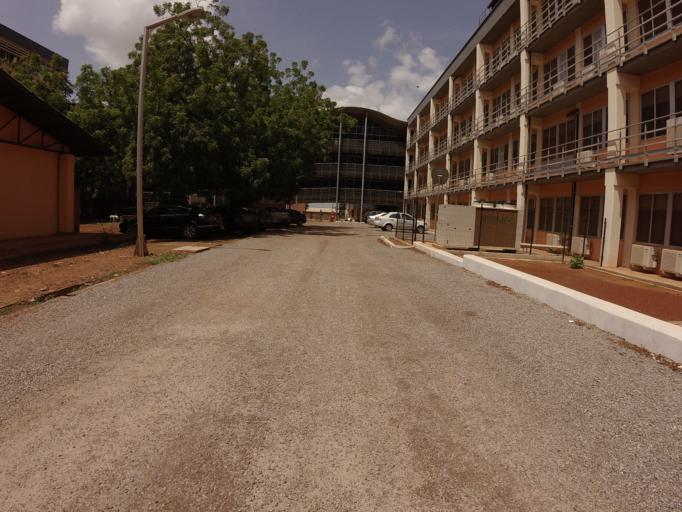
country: GH
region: Northern
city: Tamale
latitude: 9.3923
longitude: -0.8234
